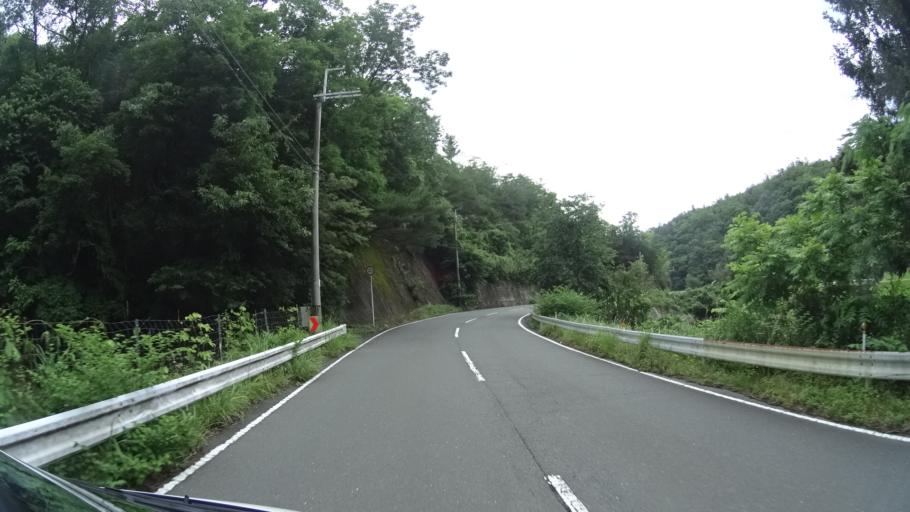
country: JP
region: Kyoto
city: Kameoka
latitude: 35.0820
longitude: 135.4114
